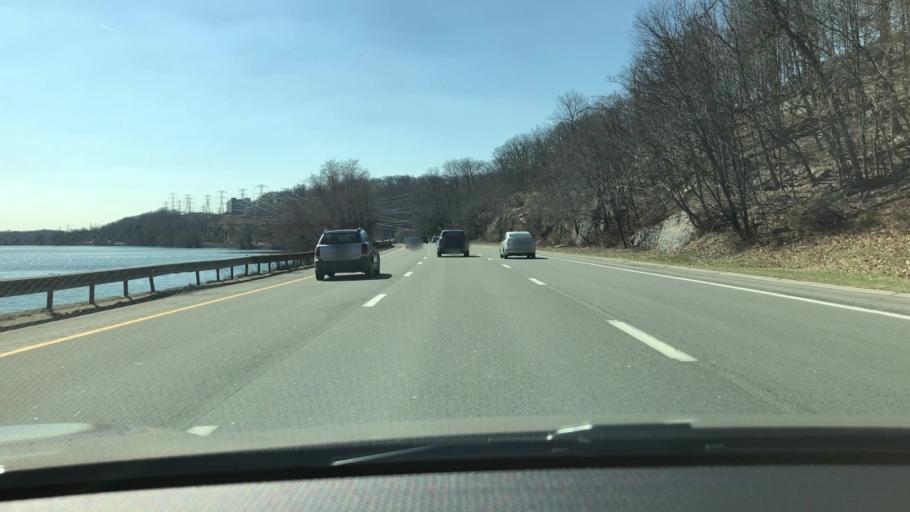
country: US
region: New York
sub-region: Westchester County
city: Hastings-on-Hudson
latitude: 40.9754
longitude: -73.8513
